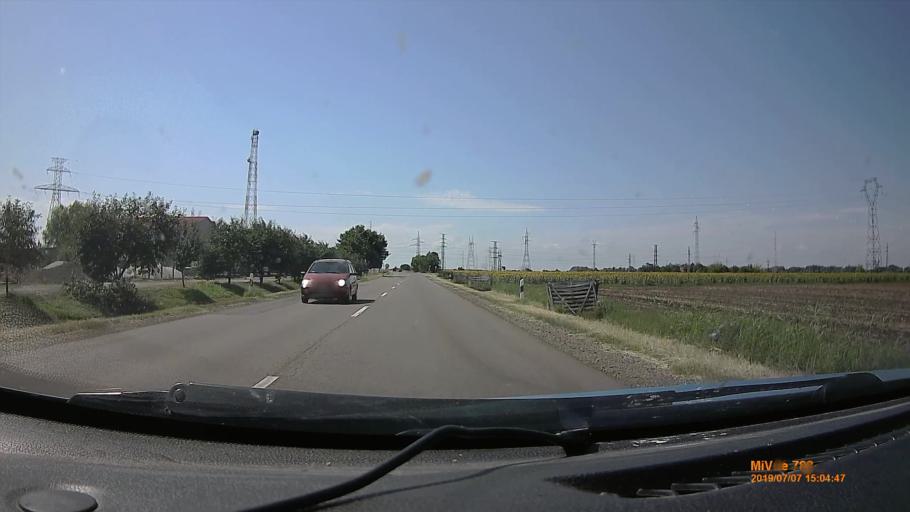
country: HU
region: Jasz-Nagykun-Szolnok
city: Szolnok
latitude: 47.2038
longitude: 20.1549
